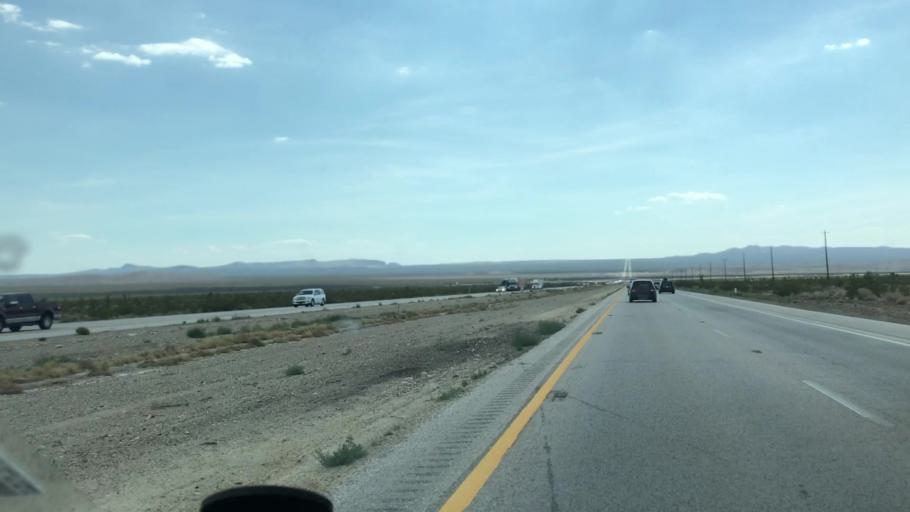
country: US
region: Nevada
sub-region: Clark County
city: Sandy Valley
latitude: 35.4556
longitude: -115.6419
